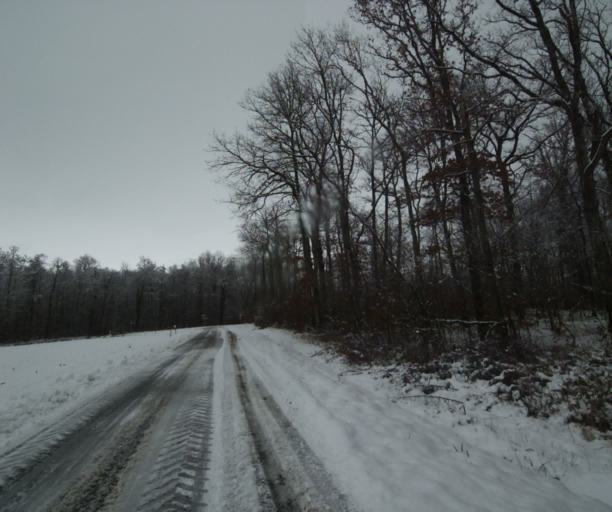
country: FR
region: Champagne-Ardenne
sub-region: Departement de la Haute-Marne
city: Wassy
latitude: 48.4593
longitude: 4.9371
